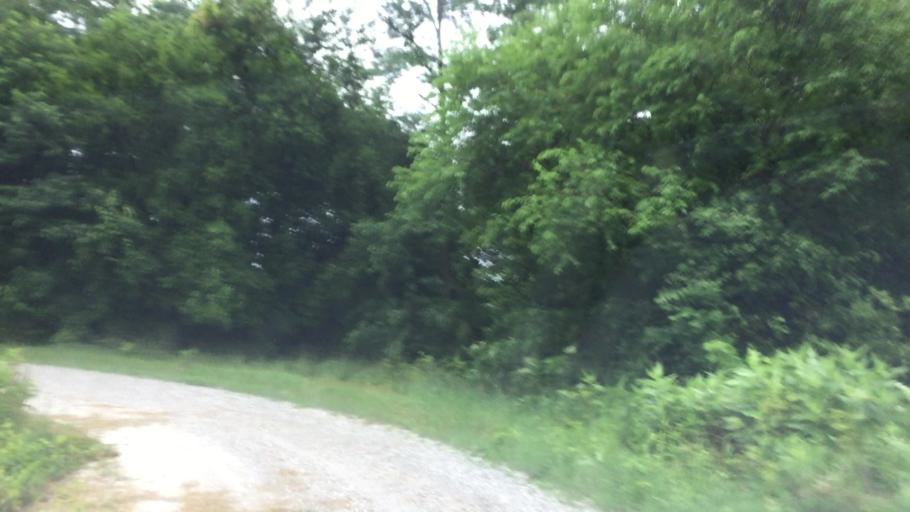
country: US
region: Illinois
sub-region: Hancock County
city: Nauvoo
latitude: 40.5493
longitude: -91.3516
